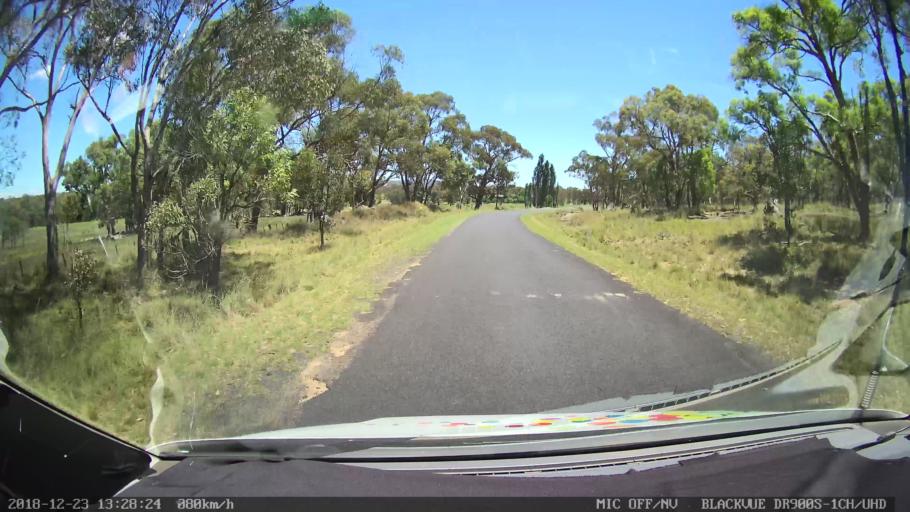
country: AU
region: New South Wales
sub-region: Armidale Dumaresq
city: Armidale
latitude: -30.4667
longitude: 151.3492
